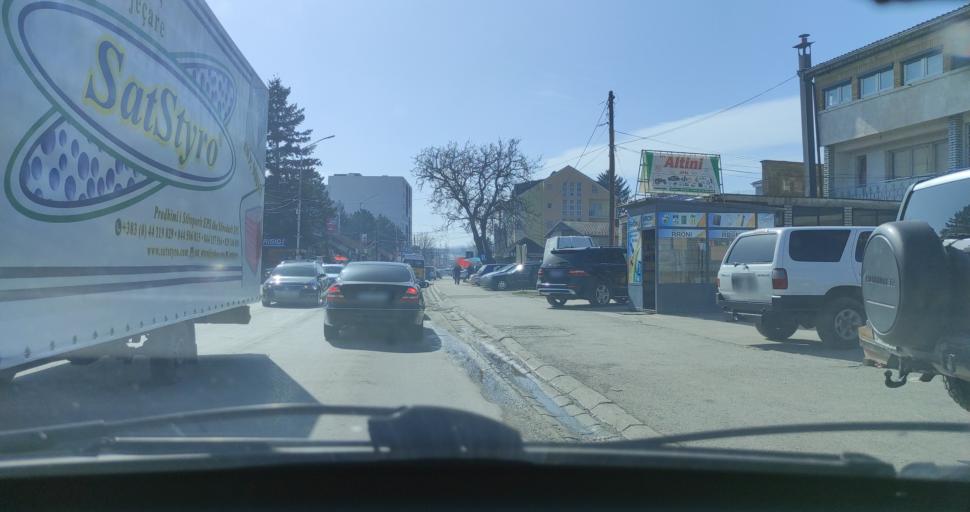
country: XK
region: Gjakova
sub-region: Komuna e Decanit
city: Decan
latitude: 42.5438
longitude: 20.2901
